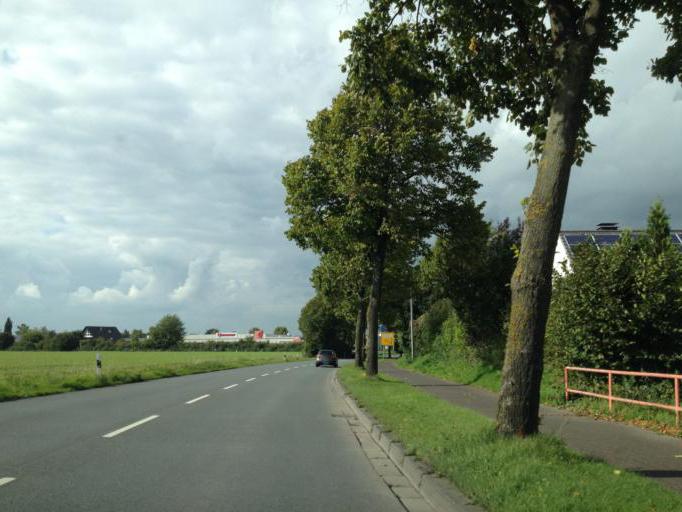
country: DE
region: North Rhine-Westphalia
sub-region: Regierungsbezirk Arnsberg
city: Soest
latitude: 51.5547
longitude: 8.0884
